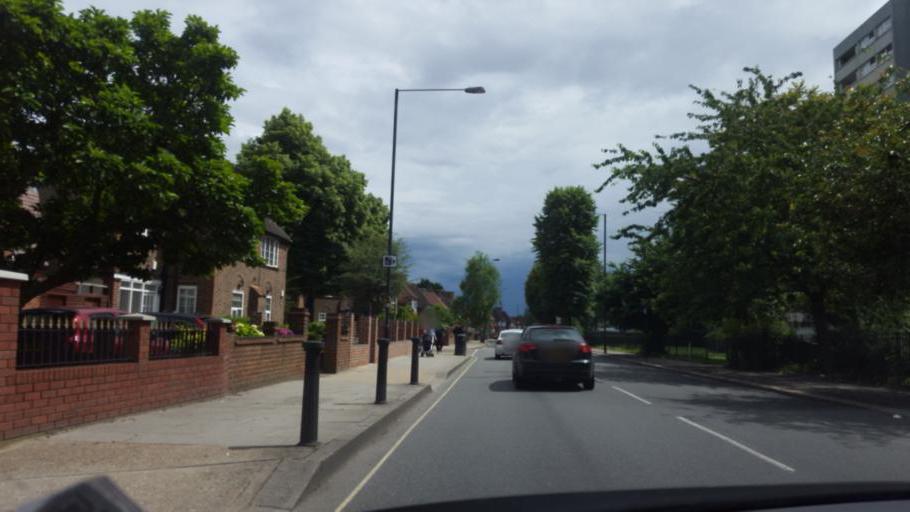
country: GB
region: England
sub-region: Greater London
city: Hammersmith
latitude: 51.5126
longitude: -0.2478
